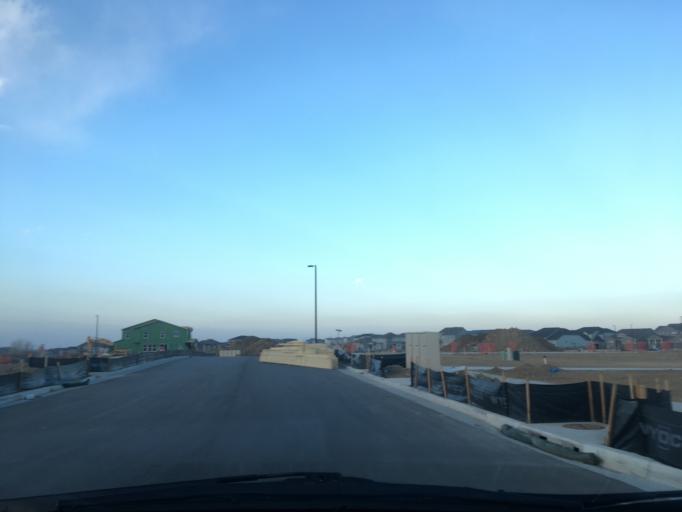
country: US
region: Colorado
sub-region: Boulder County
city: Lafayette
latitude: 40.0245
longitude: -105.0902
